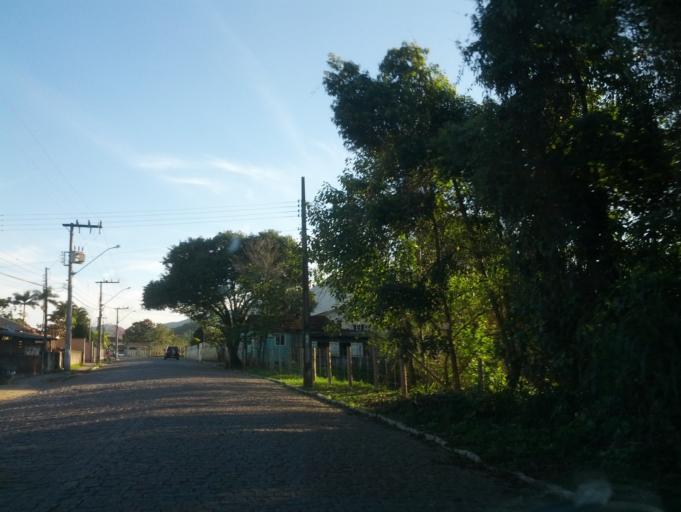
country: BR
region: Santa Catarina
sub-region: Indaial
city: Indaial
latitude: -26.8996
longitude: -49.2559
